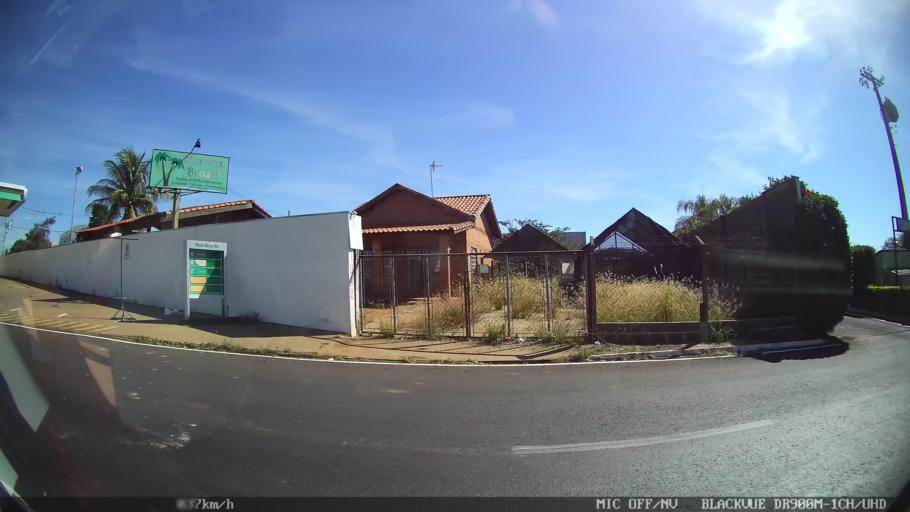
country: BR
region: Sao Paulo
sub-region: Franca
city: Franca
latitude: -20.5482
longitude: -47.4275
